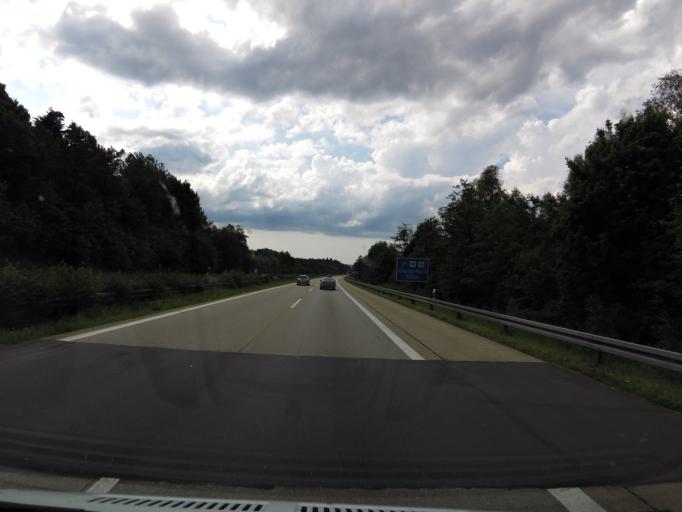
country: DE
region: Bavaria
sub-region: Lower Bavaria
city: Winzer
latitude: 48.7532
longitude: 13.0787
